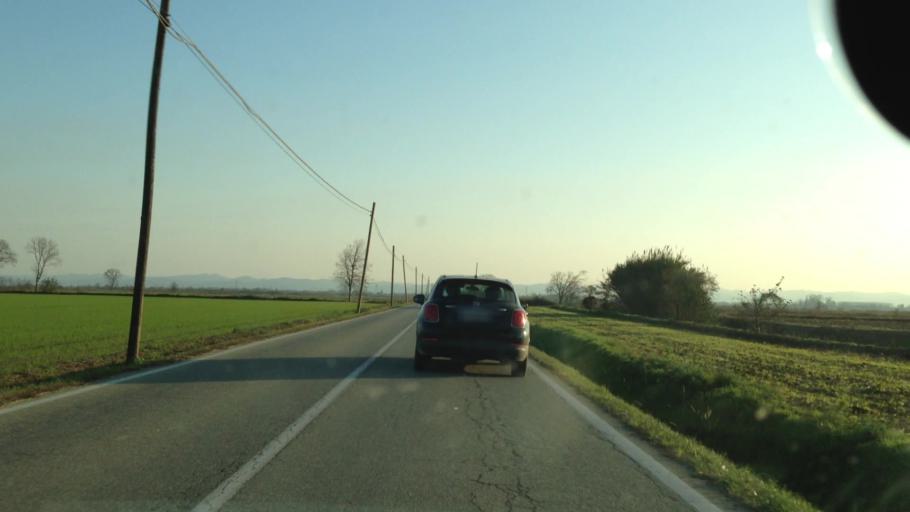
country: IT
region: Piedmont
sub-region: Provincia di Vercelli
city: Livorno Ferraris
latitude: 45.2697
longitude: 8.0821
